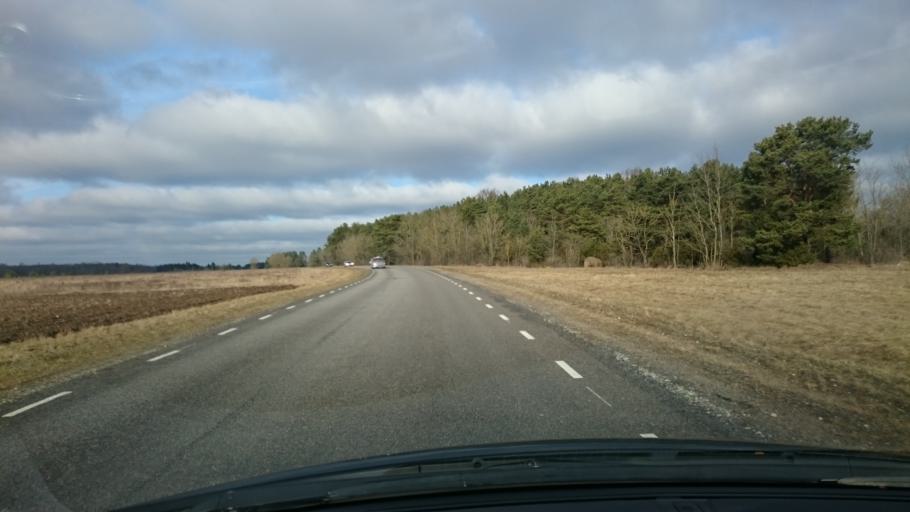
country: EE
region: Harju
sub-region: Keila linn
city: Keila
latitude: 59.3400
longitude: 24.3703
